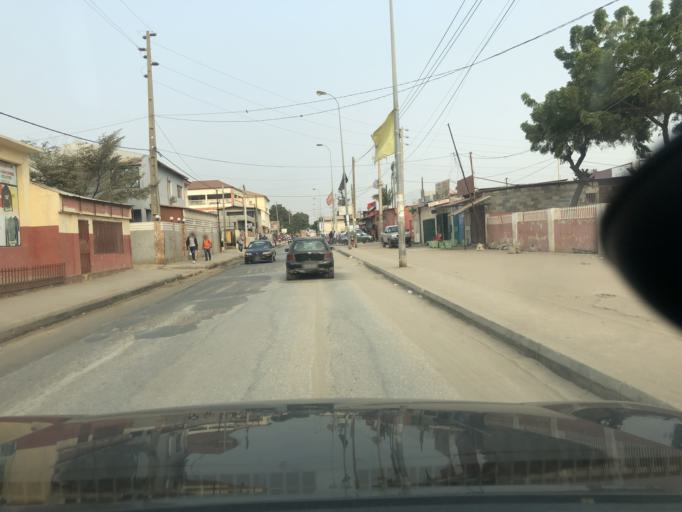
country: AO
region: Luanda
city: Luanda
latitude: -8.8834
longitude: 13.2014
